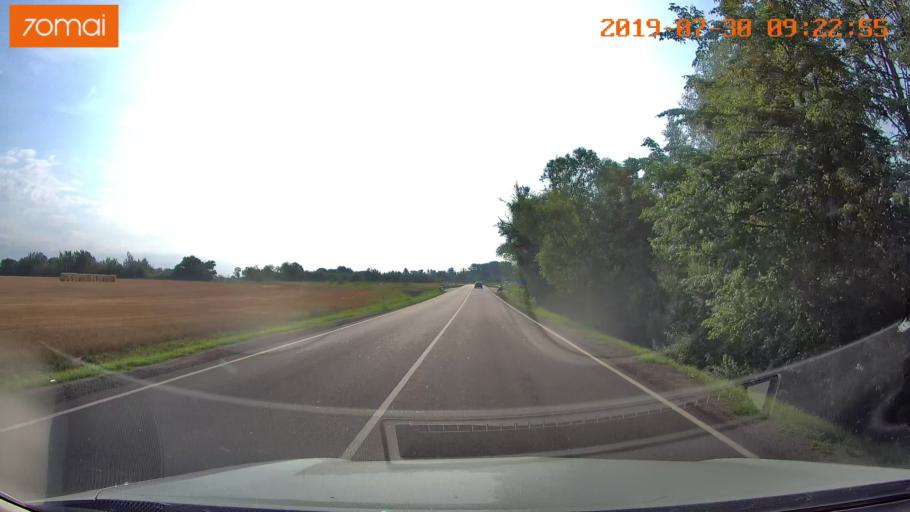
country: RU
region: Kaliningrad
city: Nesterov
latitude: 54.6335
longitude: 22.6649
